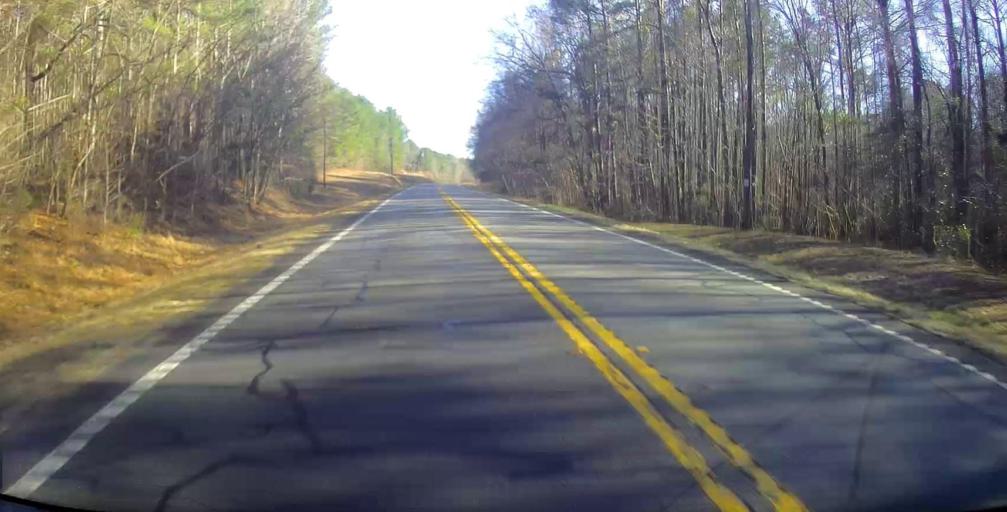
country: US
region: Georgia
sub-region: Talbot County
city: Talbotton
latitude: 32.7073
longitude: -84.5548
